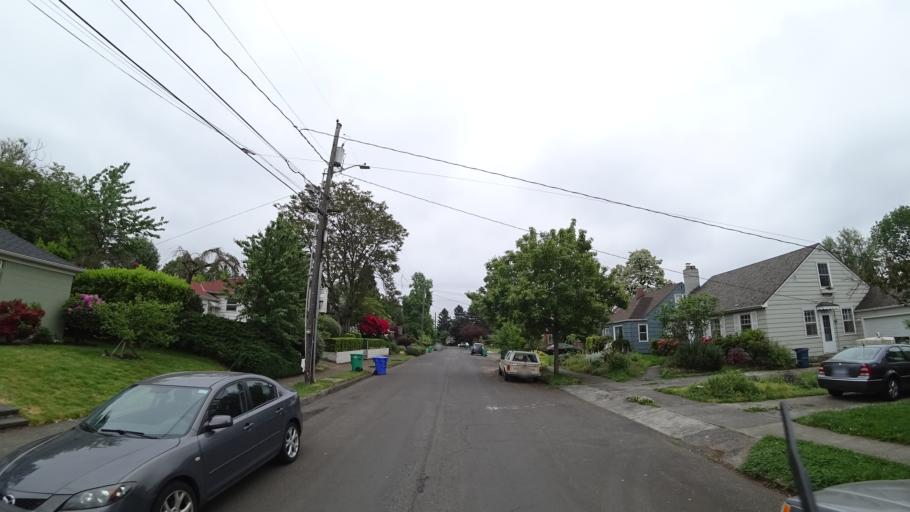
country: US
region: Oregon
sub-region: Multnomah County
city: Lents
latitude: 45.5028
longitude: -122.6021
